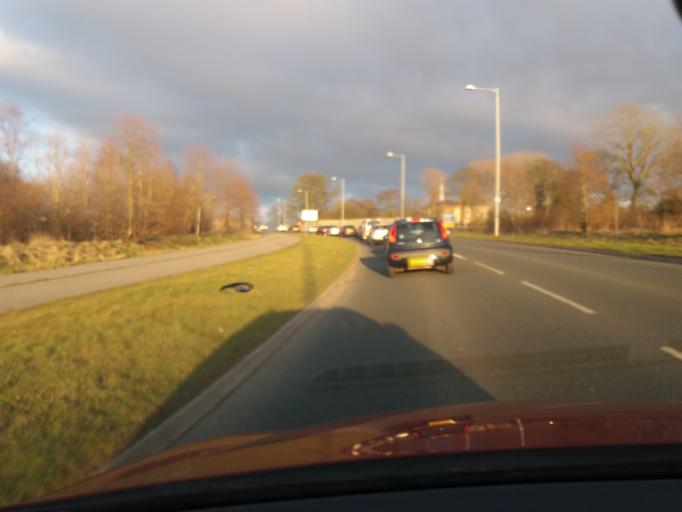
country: GB
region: England
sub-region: Lancashire
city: Chorley
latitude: 53.6729
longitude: -2.6371
